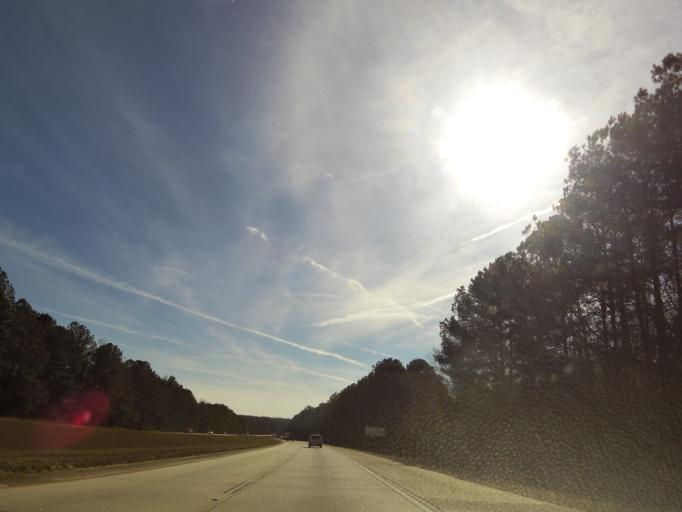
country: US
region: Georgia
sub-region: Troup County
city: Hogansville
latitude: 33.1082
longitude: -84.9059
